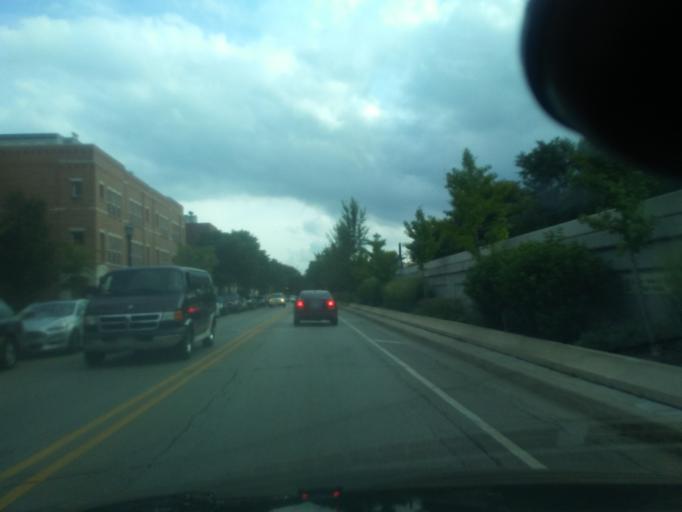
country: US
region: Illinois
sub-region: Cook County
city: Evanston
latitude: 42.0291
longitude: -87.6784
